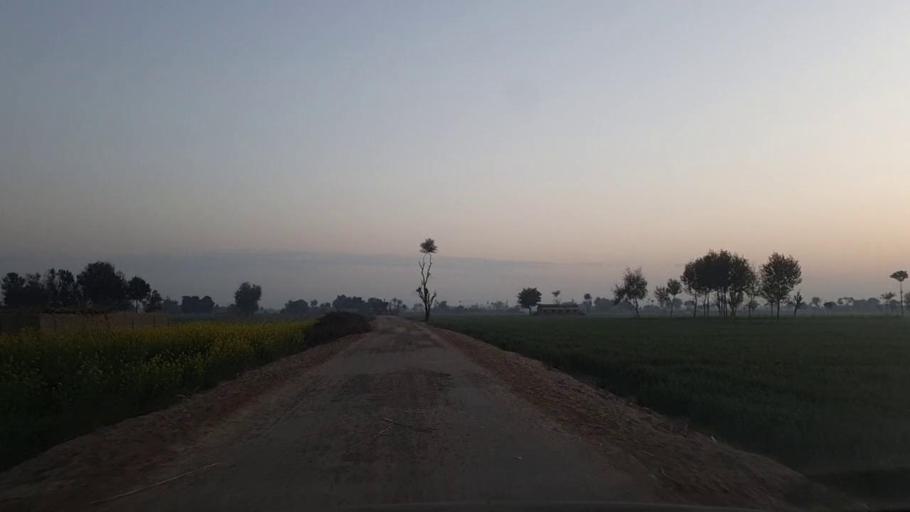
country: PK
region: Sindh
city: Daur
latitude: 26.4793
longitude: 68.4875
